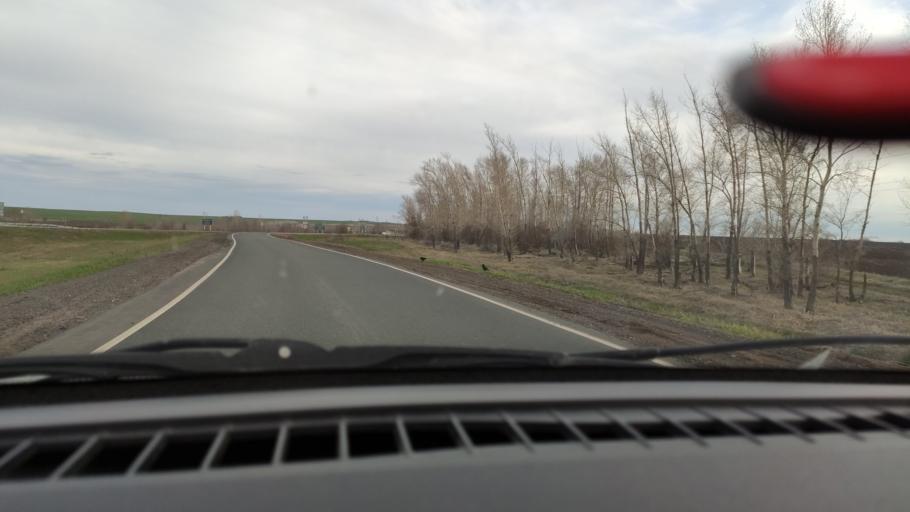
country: RU
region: Orenburg
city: Sakmara
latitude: 52.1737
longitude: 55.2908
